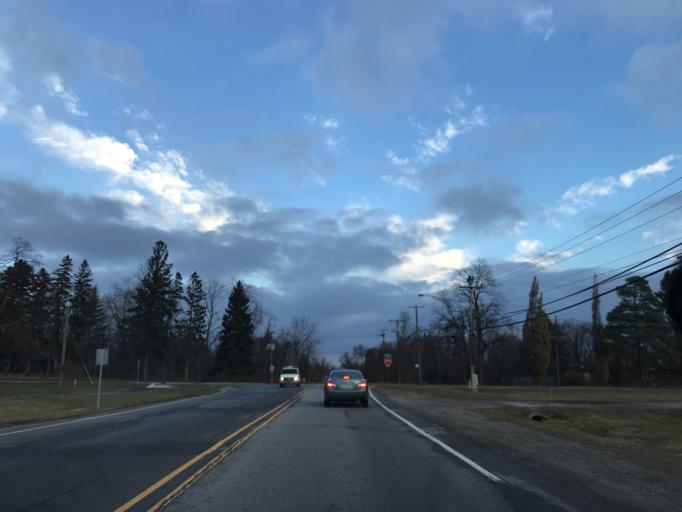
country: US
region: Michigan
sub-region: Oakland County
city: Novi
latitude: 42.4797
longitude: -83.4955
